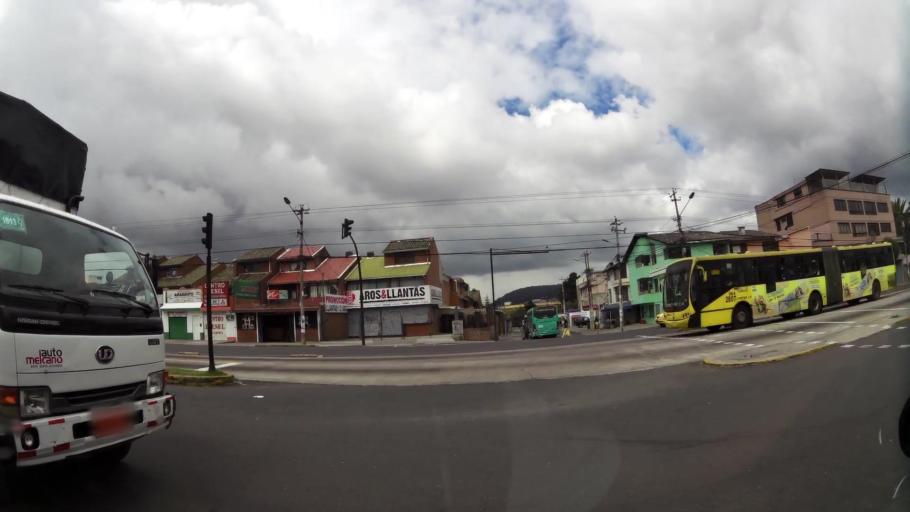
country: EC
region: Pichincha
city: Quito
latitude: -0.1627
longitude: -78.4873
